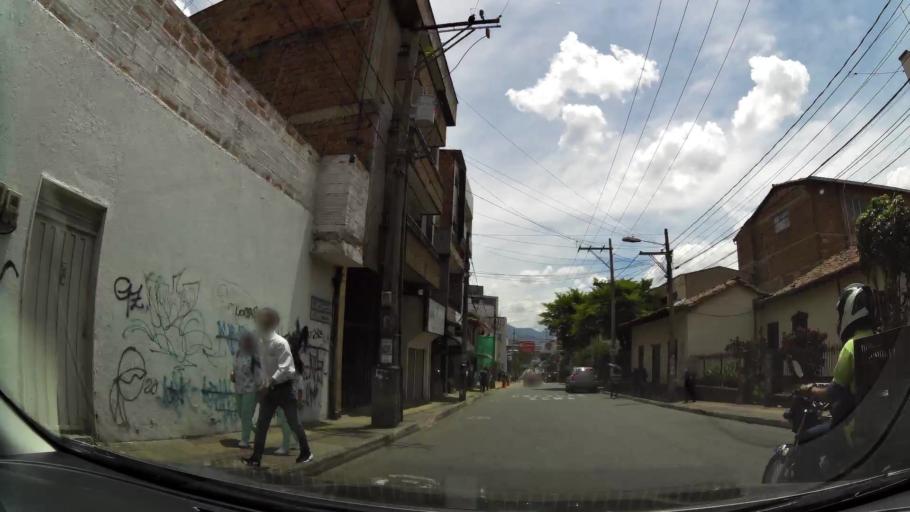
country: CO
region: Antioquia
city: Bello
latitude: 6.3343
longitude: -75.5584
